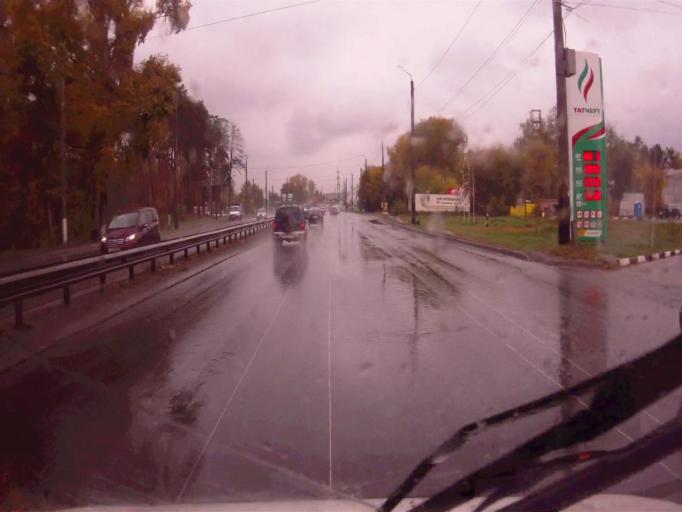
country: RU
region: Chelyabinsk
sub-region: Gorod Chelyabinsk
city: Chelyabinsk
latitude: 55.2348
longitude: 61.3661
